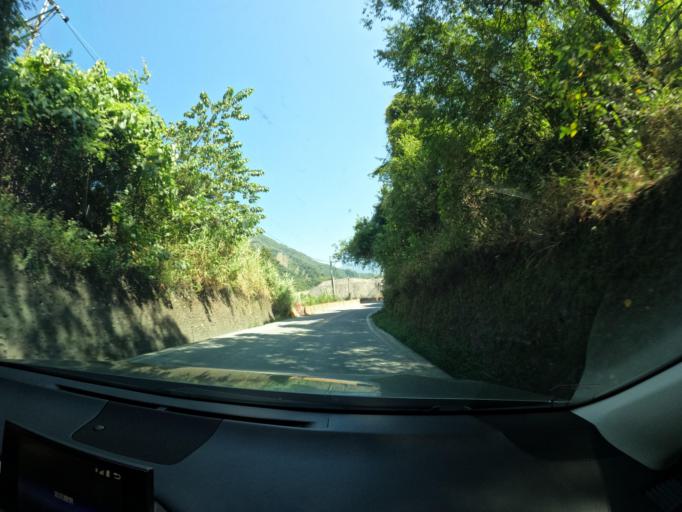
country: TW
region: Taiwan
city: Yujing
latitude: 23.1824
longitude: 120.7812
